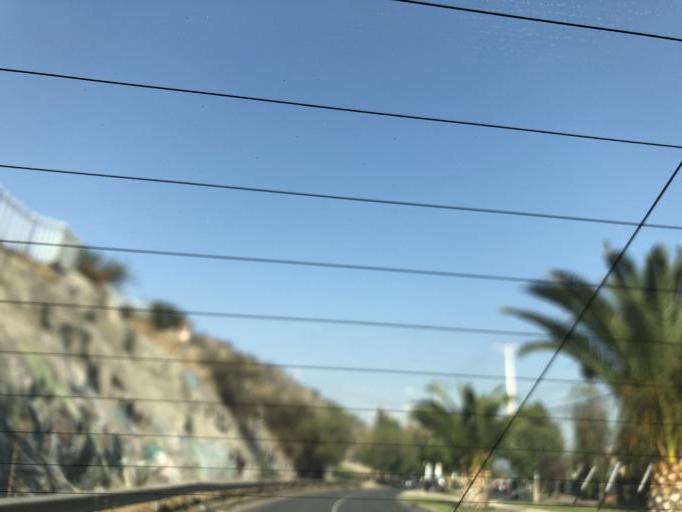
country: CL
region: Santiago Metropolitan
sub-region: Provincia de Cordillera
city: Puente Alto
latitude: -33.5972
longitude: -70.5572
